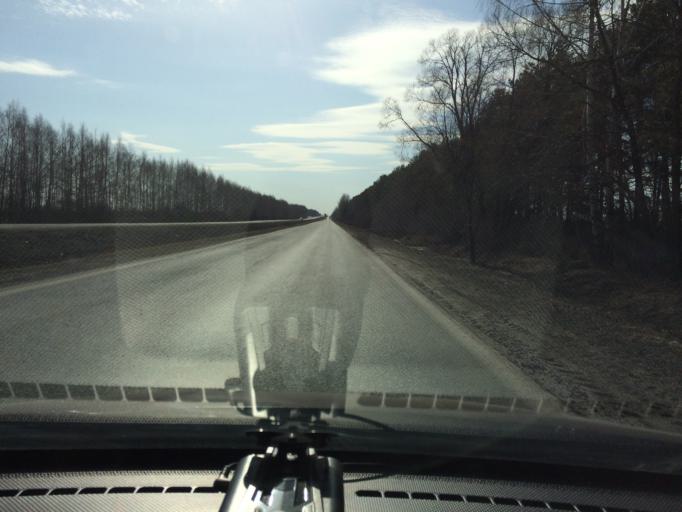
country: RU
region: Mariy-El
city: Yoshkar-Ola
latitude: 56.7341
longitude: 48.1592
